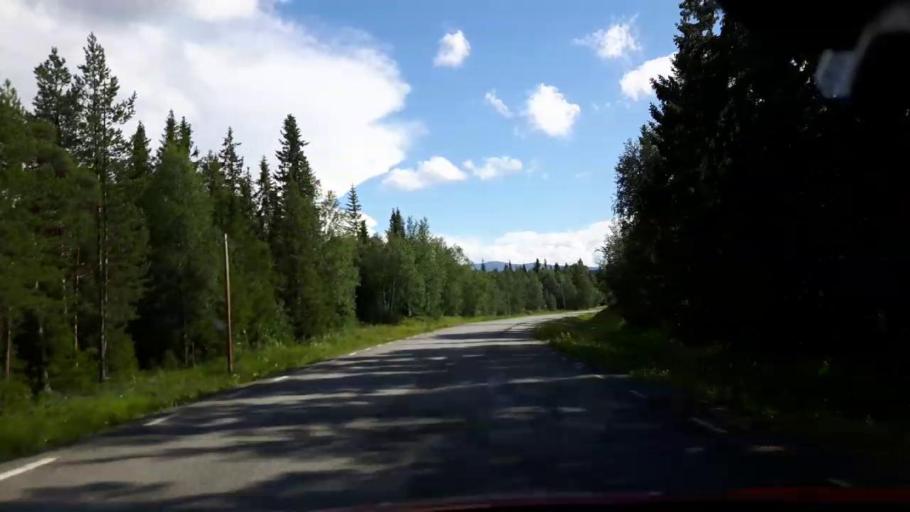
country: SE
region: Jaemtland
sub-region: Are Kommun
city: Are
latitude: 63.2075
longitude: 13.1621
